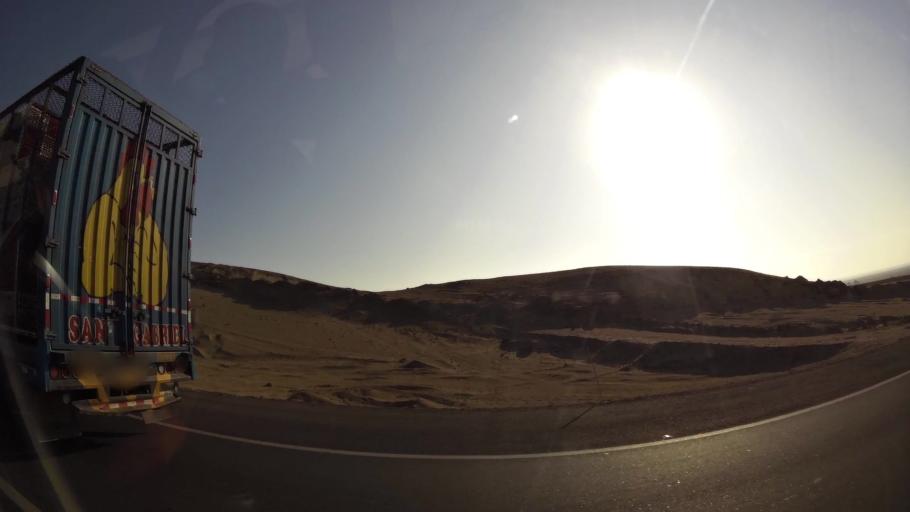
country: PE
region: Ica
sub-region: Provincia de Pisco
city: San Clemente
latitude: -13.6377
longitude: -76.1732
